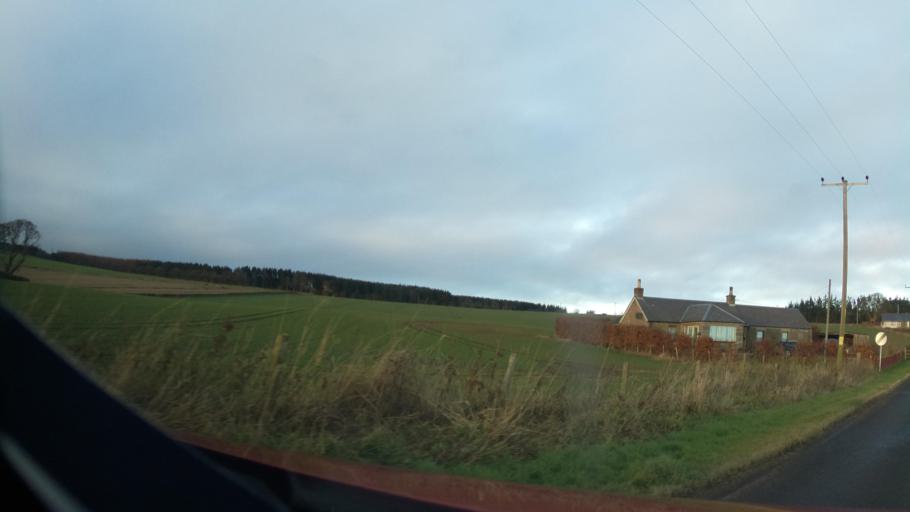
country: GB
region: Scotland
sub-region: Fife
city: Tayport
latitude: 56.5179
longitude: -2.8166
